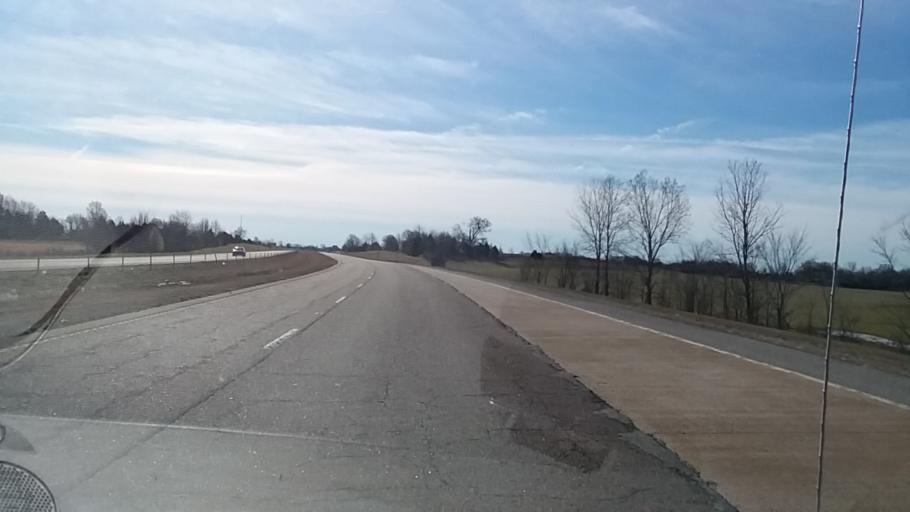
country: US
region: Tennessee
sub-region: Crockett County
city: Alamo
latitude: 35.7911
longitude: -89.1564
